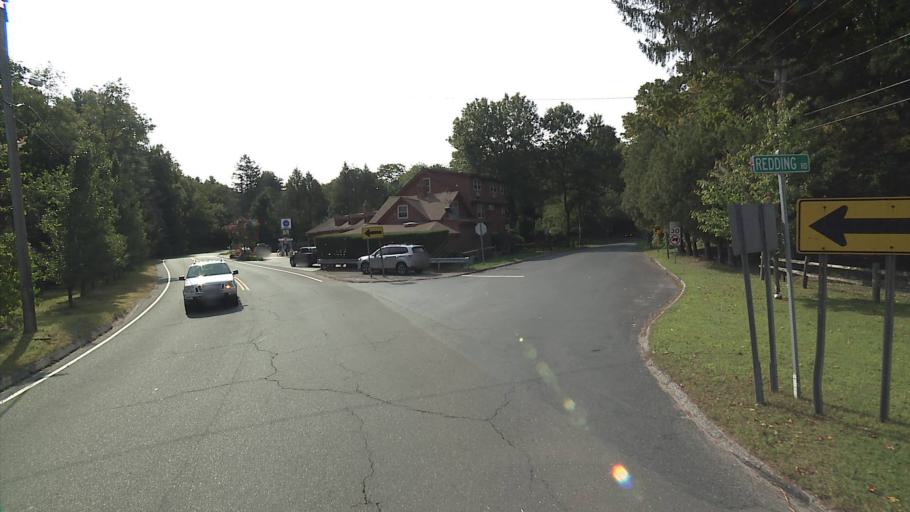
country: US
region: Connecticut
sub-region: Fairfield County
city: Westport
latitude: 41.2324
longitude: -73.3212
